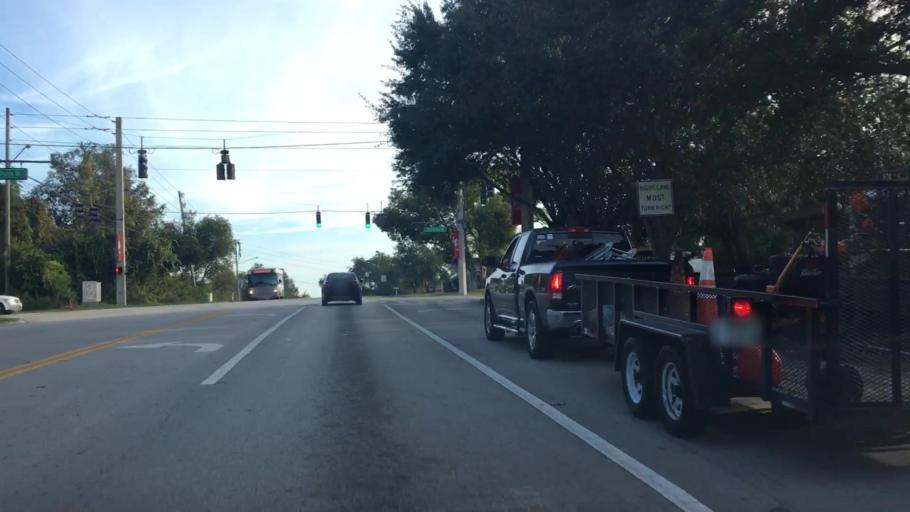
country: US
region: Florida
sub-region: Volusia County
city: Deltona
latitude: 28.9074
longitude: -81.2249
